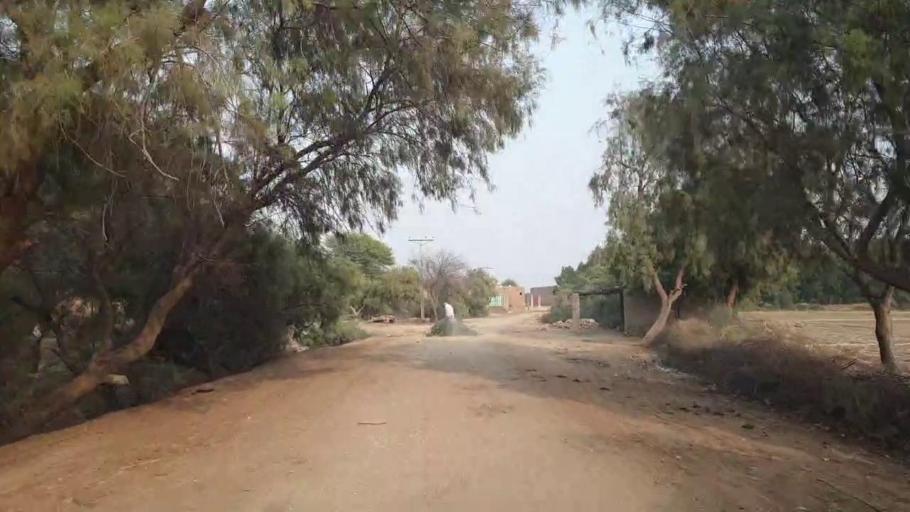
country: PK
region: Sindh
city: Sann
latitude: 26.1080
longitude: 68.0830
